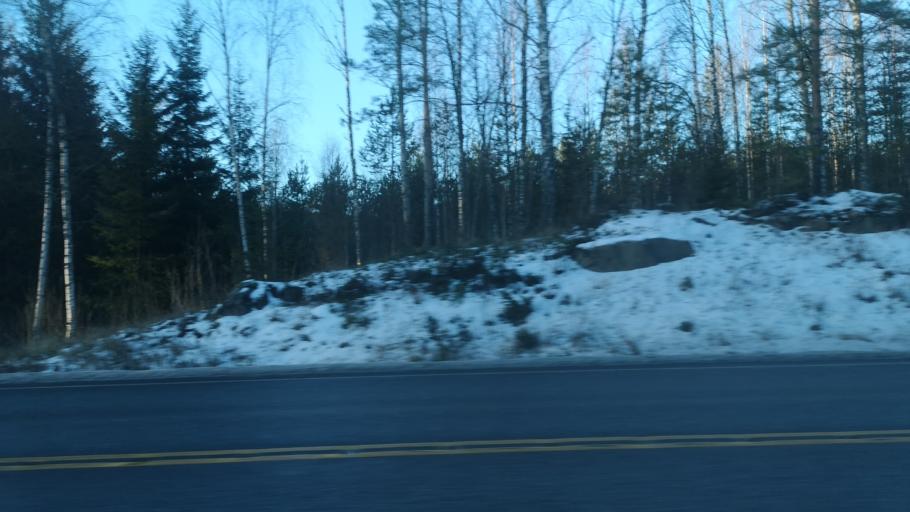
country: FI
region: Southern Savonia
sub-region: Mikkeli
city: Mikkeli
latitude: 61.7436
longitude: 27.5326
